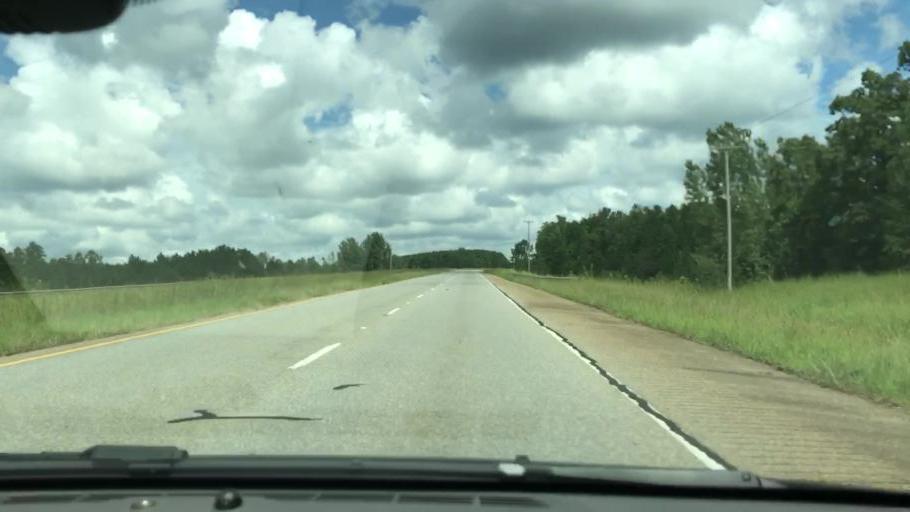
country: US
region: Georgia
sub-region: Stewart County
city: Lumpkin
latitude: 32.1083
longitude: -84.8135
